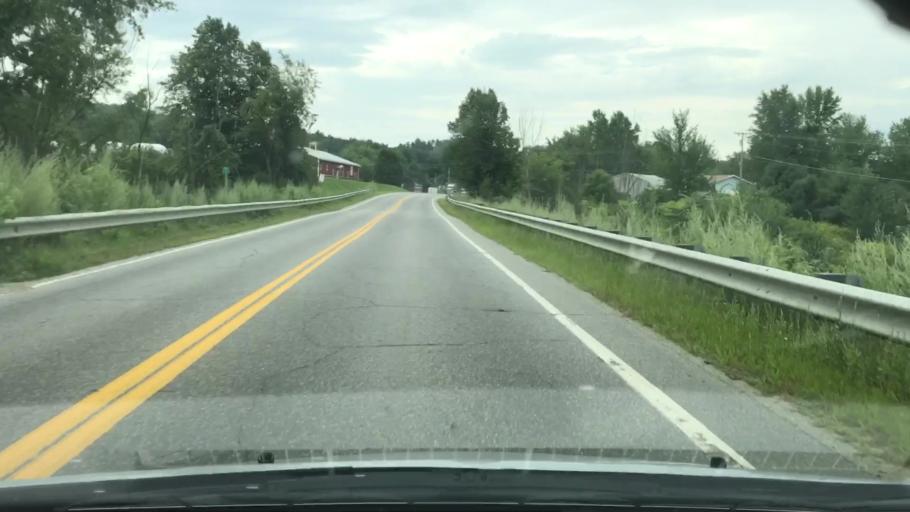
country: US
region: New Hampshire
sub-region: Grafton County
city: North Haverhill
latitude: 44.0796
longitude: -72.0272
